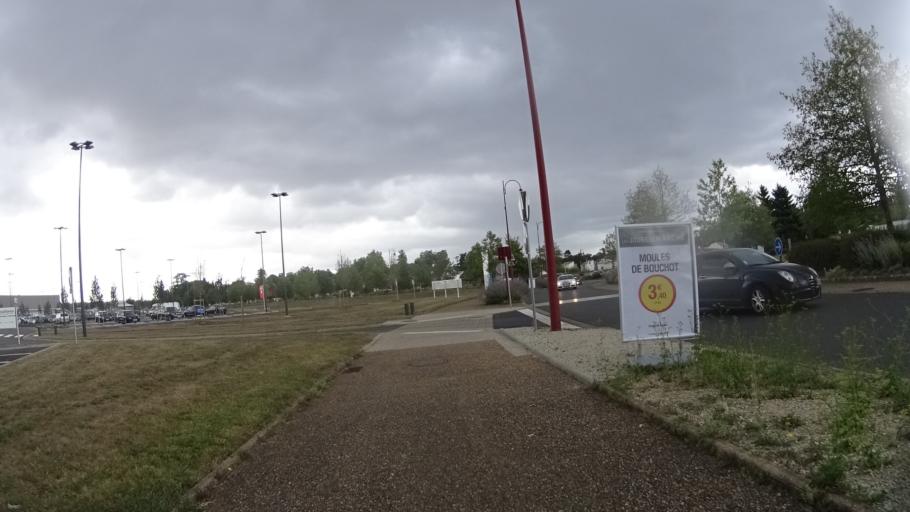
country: FR
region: Centre
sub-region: Departement du Loiret
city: Saint-Pryve-Saint-Mesmin
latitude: 47.8809
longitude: 1.8648
